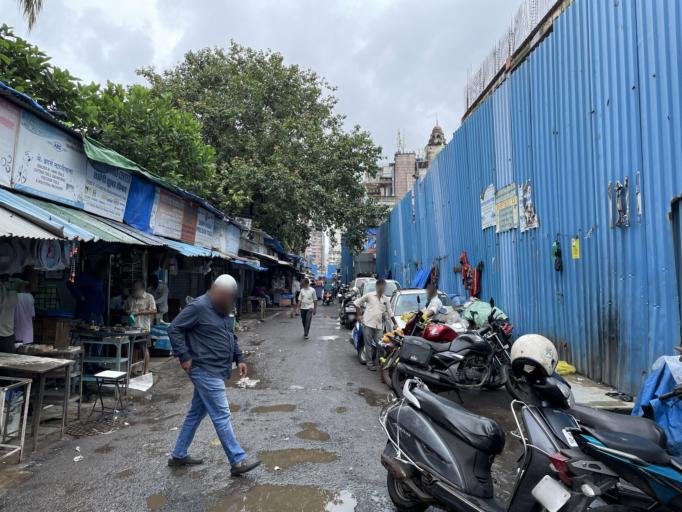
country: IN
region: Maharashtra
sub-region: Mumbai Suburban
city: Mumbai
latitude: 18.9586
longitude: 72.8299
